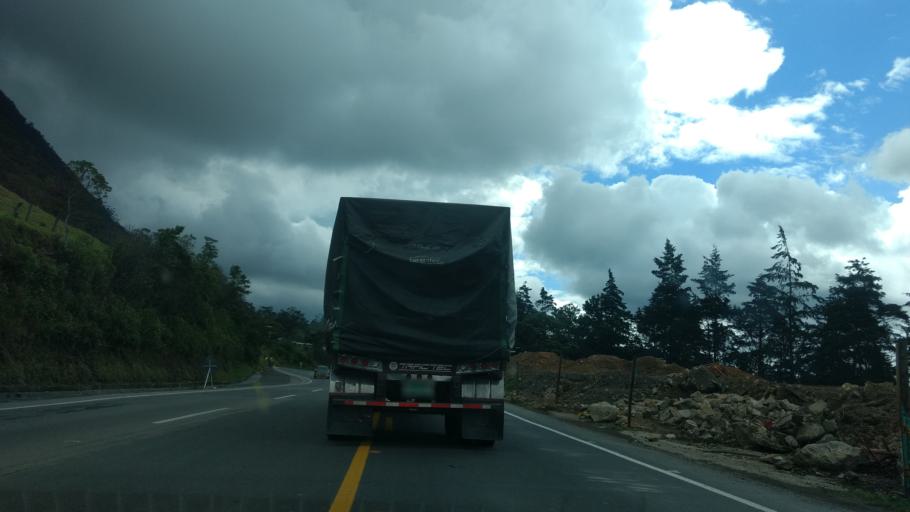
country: CO
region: Cundinamarca
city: San Francisco
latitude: 4.9313
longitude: -74.2978
